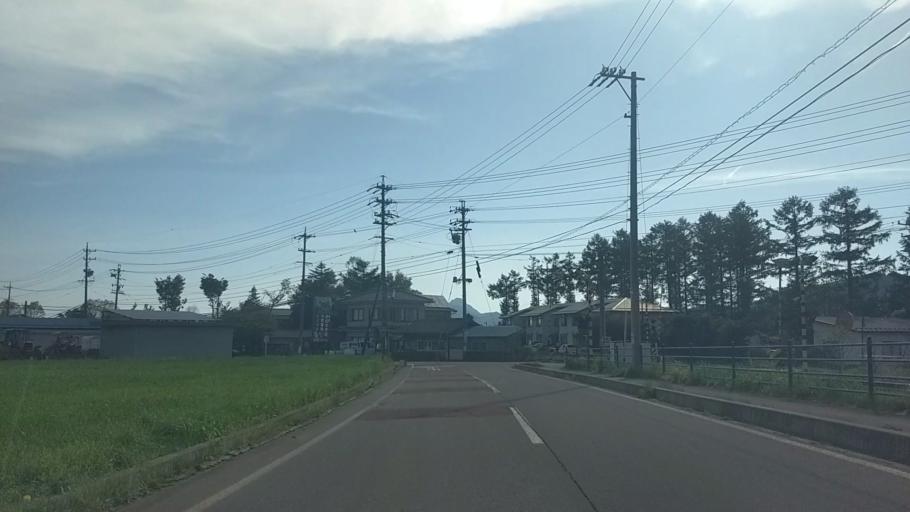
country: JP
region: Yamanashi
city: Nirasaki
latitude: 35.9514
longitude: 138.4719
